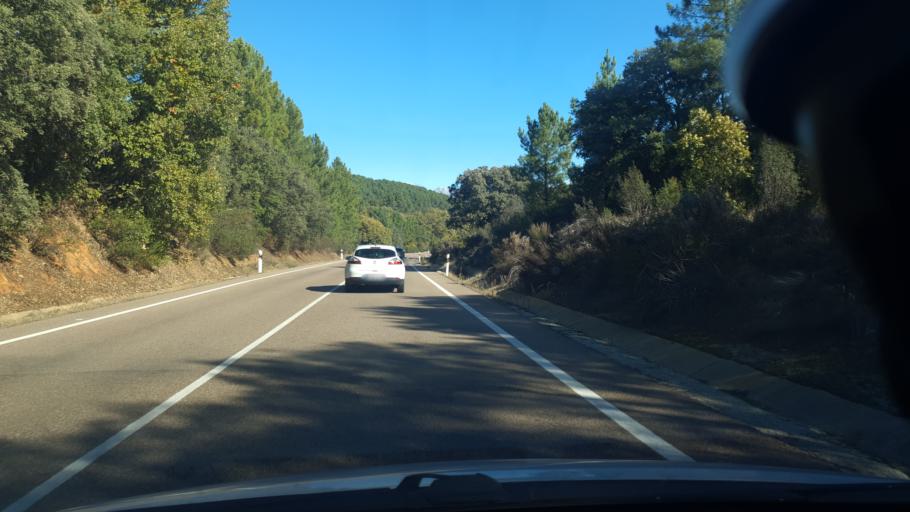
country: ES
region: Castille and Leon
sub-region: Provincia de Avila
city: Arenas de San Pedro
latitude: 40.1674
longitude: -5.1031
